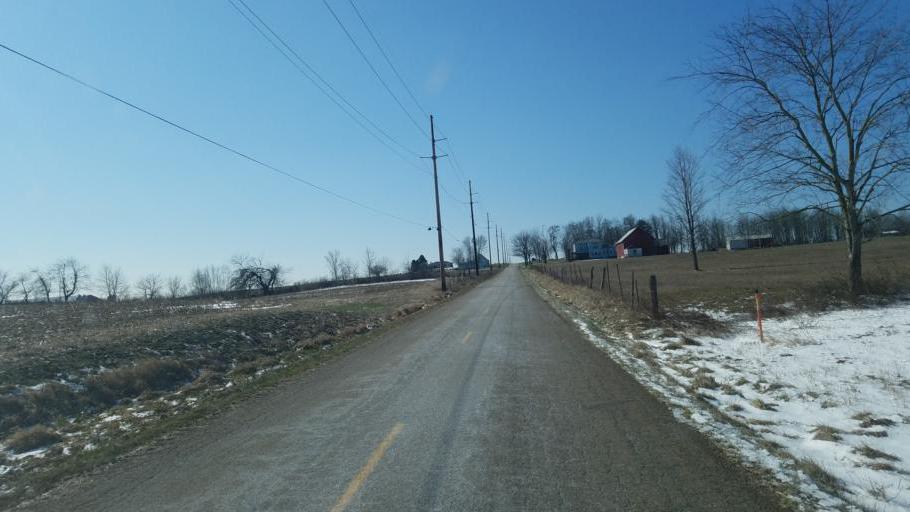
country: US
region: Ohio
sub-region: Licking County
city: Utica
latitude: 40.2904
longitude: -82.4741
